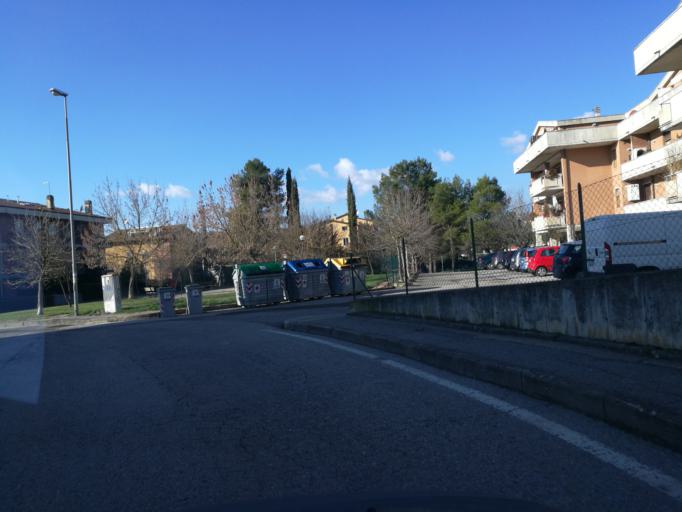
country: IT
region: Umbria
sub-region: Provincia di Perugia
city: Perugia
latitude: 43.0813
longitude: 12.3678
